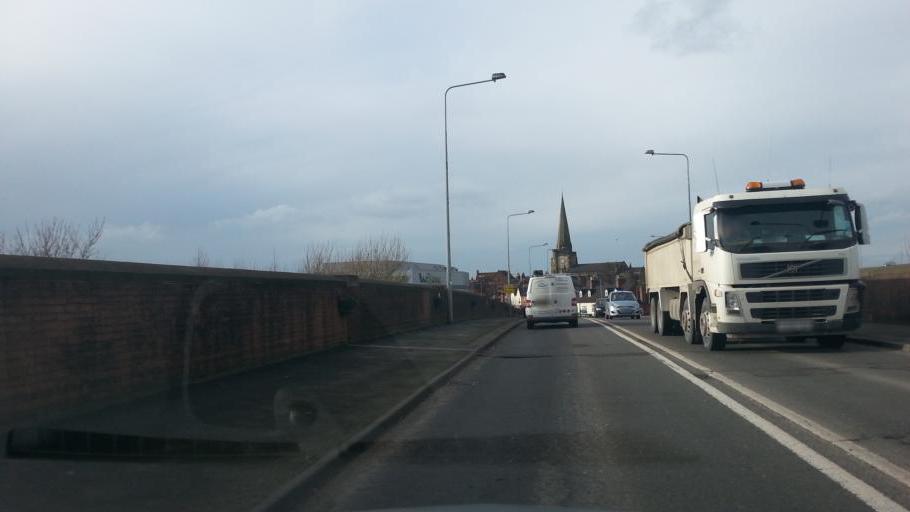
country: GB
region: England
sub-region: Staffordshire
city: Uttoxeter
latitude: 52.8961
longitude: -1.8599
